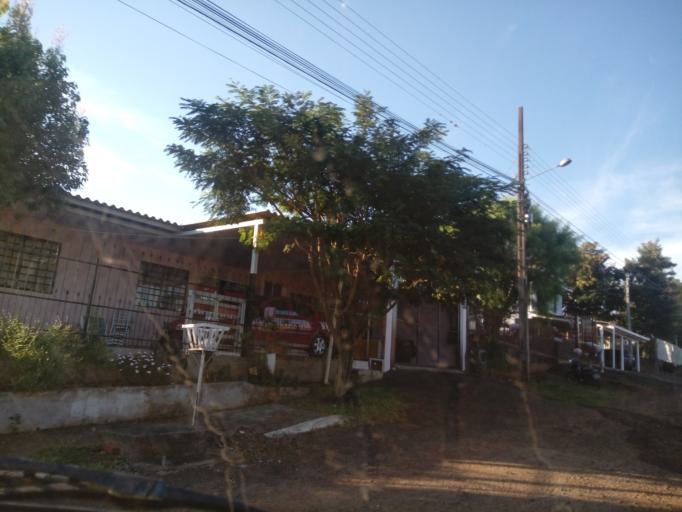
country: BR
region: Santa Catarina
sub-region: Chapeco
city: Chapeco
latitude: -27.0351
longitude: -52.6312
